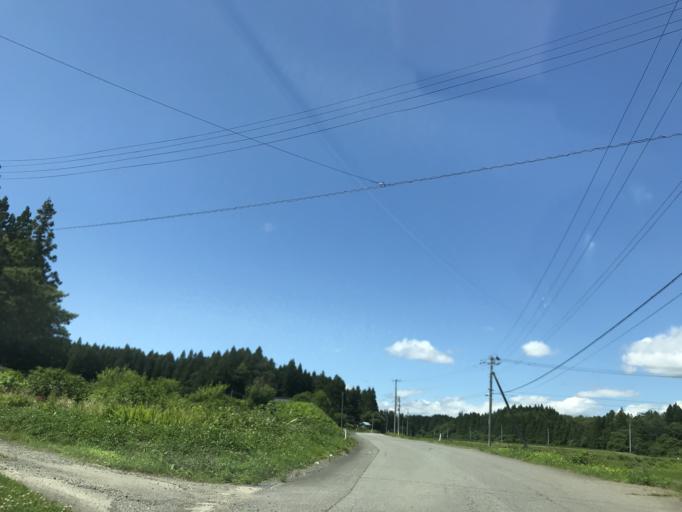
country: JP
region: Iwate
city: Ichinoseki
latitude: 38.9271
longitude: 141.0197
